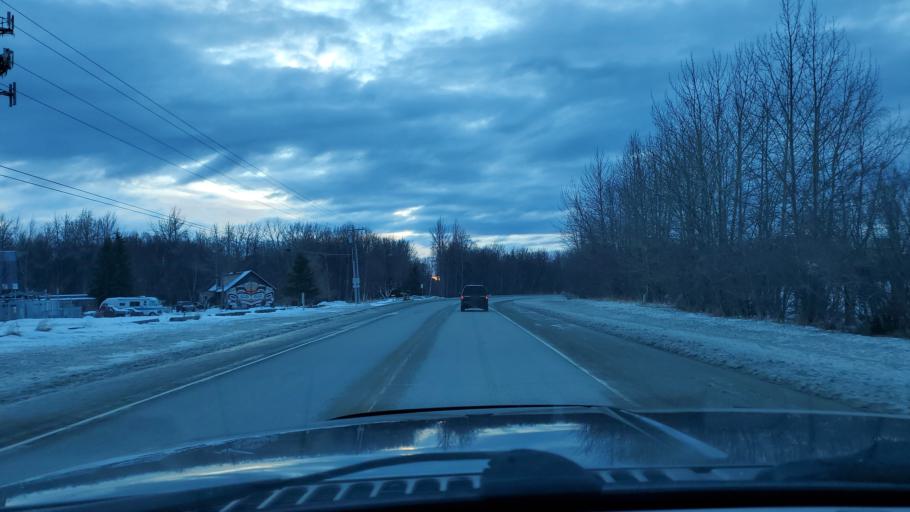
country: US
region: Alaska
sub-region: Matanuska-Susitna Borough
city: Farm Loop
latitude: 61.6584
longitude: -149.0958
